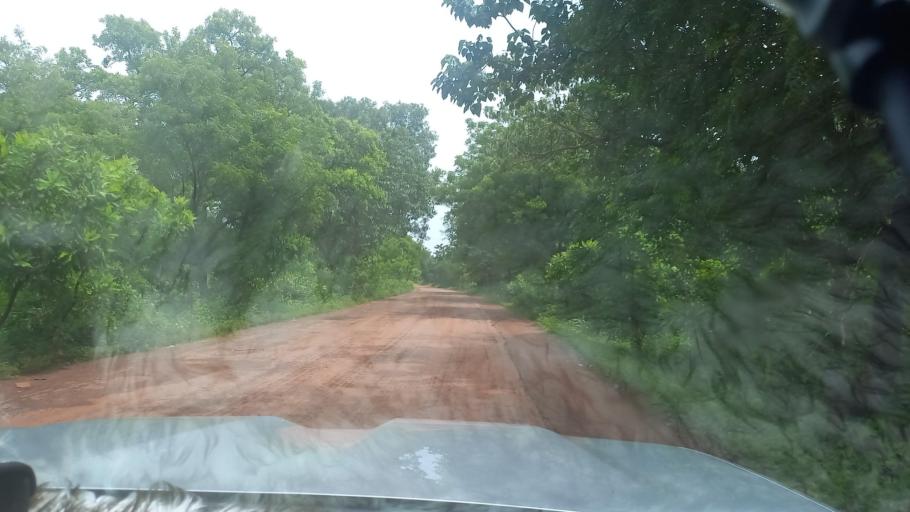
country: SN
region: Kolda
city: Marsassoum
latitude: 12.9138
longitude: -16.0135
